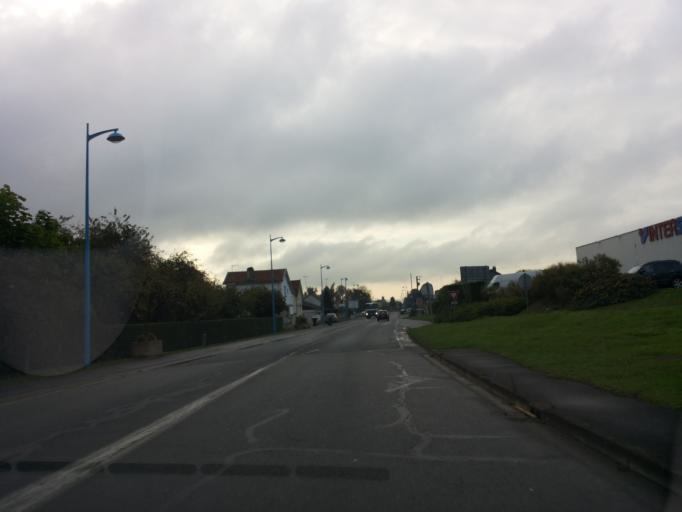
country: FR
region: Champagne-Ardenne
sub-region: Departement des Ardennes
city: Villers-Semeuse
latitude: 49.7311
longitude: 4.7528
